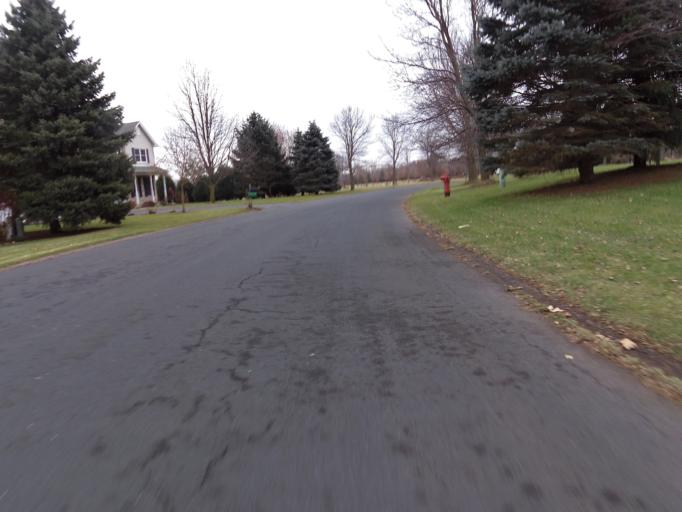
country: US
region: Minnesota
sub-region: Washington County
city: Lake Elmo
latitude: 44.9899
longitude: -92.8664
